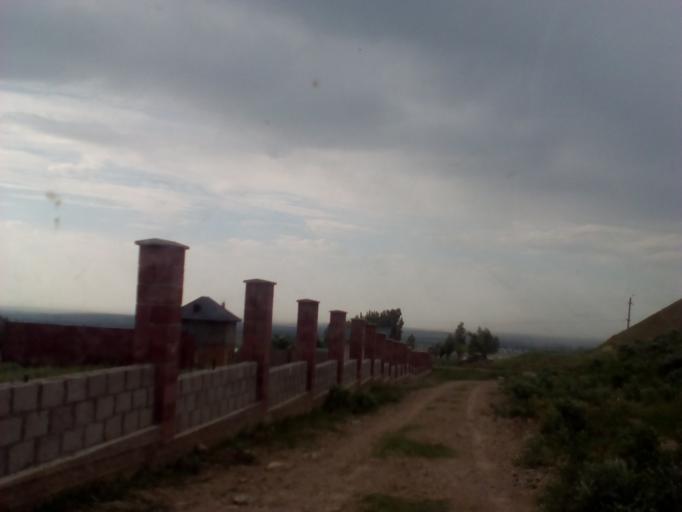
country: KZ
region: Almaty Oblysy
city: Burunday
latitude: 43.1486
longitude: 76.3858
